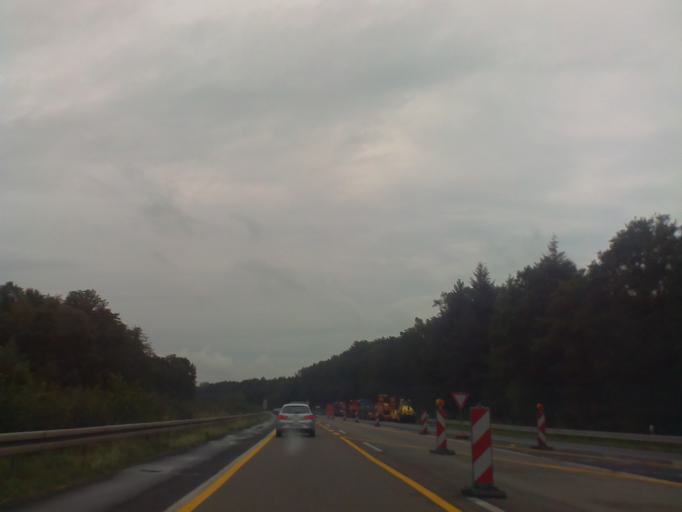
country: DE
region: Hesse
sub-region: Regierungsbezirk Darmstadt
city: Erlensee
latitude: 50.1279
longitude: 8.9810
